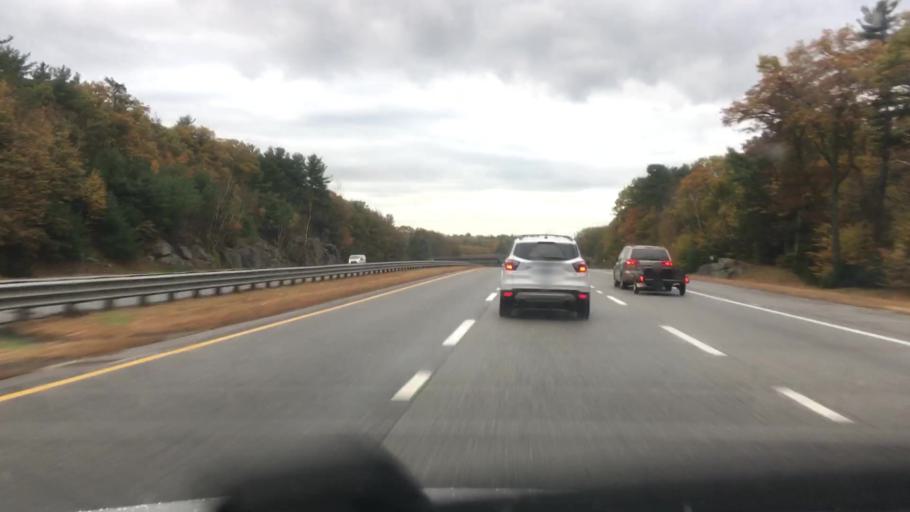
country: US
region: Maine
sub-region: York County
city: Cape Neddick
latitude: 43.2268
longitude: -70.6368
